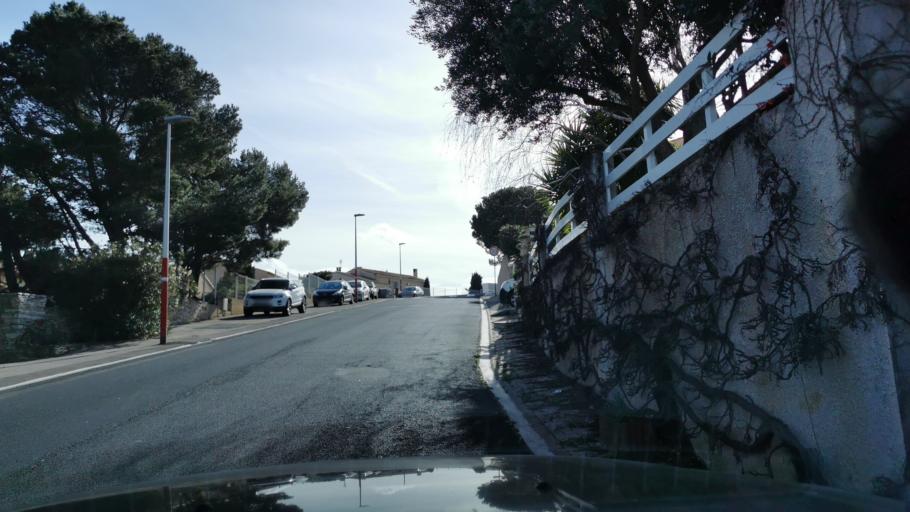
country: FR
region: Languedoc-Roussillon
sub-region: Departement de l'Aude
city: Narbonne
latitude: 43.1656
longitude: 2.9775
